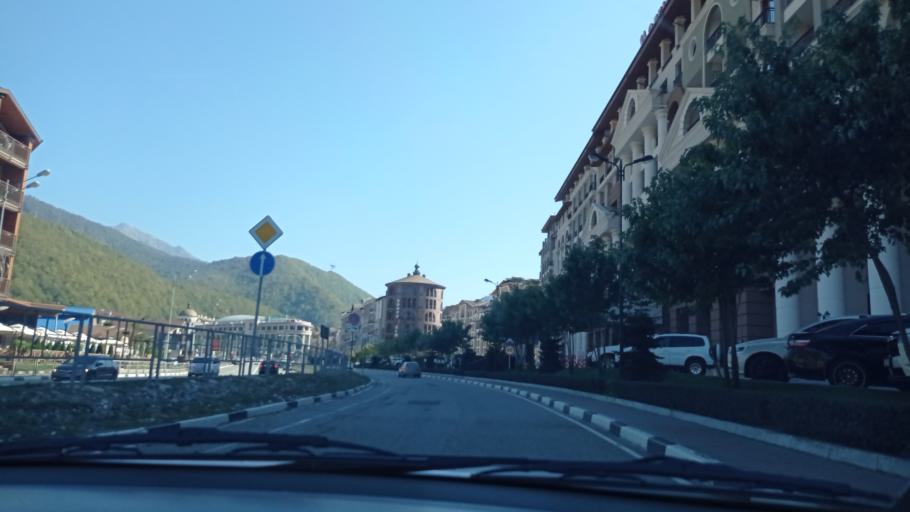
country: RU
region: Krasnodarskiy
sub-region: Sochi City
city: Krasnaya Polyana
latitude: 43.6842
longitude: 40.2563
